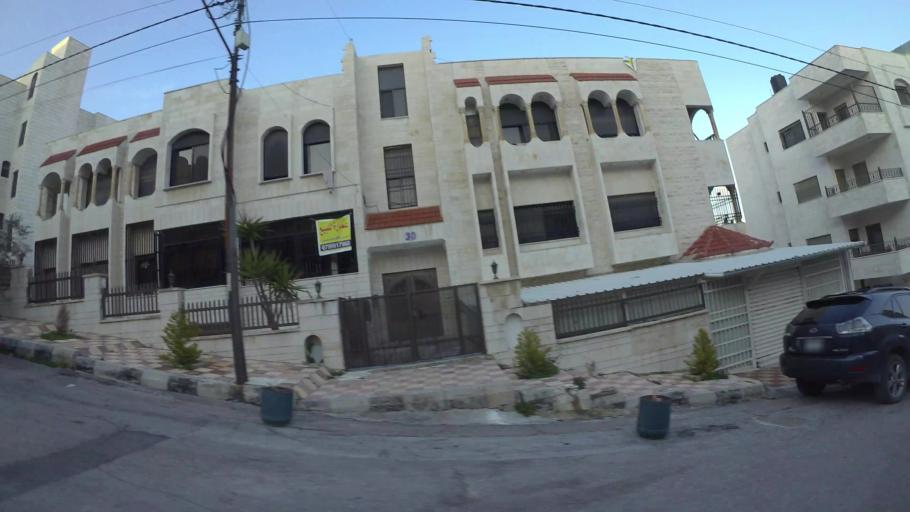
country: JO
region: Amman
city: Al Jubayhah
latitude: 31.9905
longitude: 35.8777
